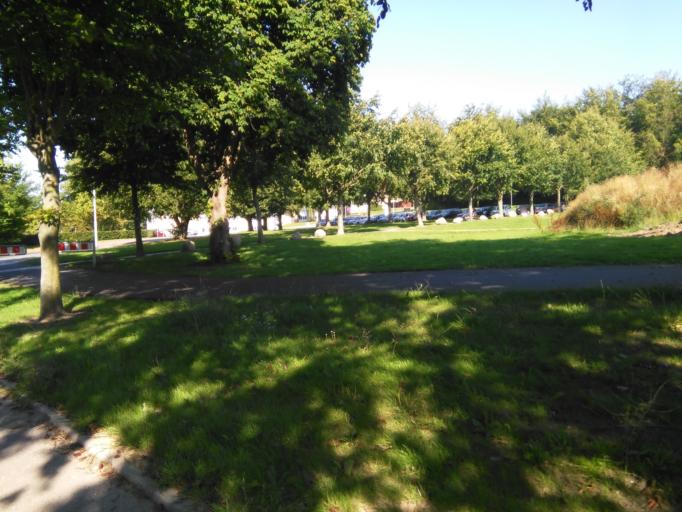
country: DK
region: Central Jutland
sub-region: Arhus Kommune
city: Stavtrup
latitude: 56.1491
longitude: 10.1369
